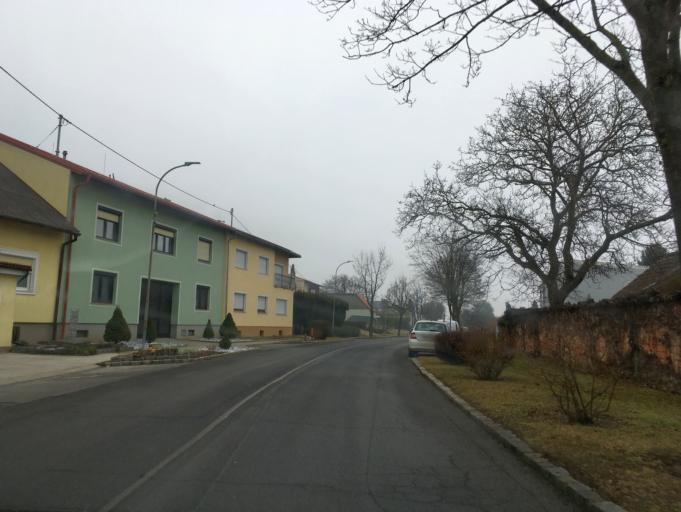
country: AT
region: Lower Austria
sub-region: Politischer Bezirk Bruck an der Leitha
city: Trautmannsdorf an der Leitha
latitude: 48.0529
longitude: 16.6467
